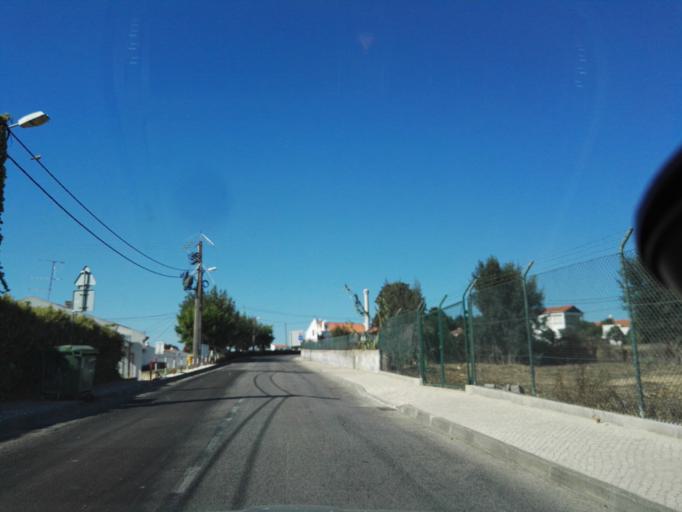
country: PT
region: Santarem
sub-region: Benavente
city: Poceirao
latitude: 38.8645
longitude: -8.7509
